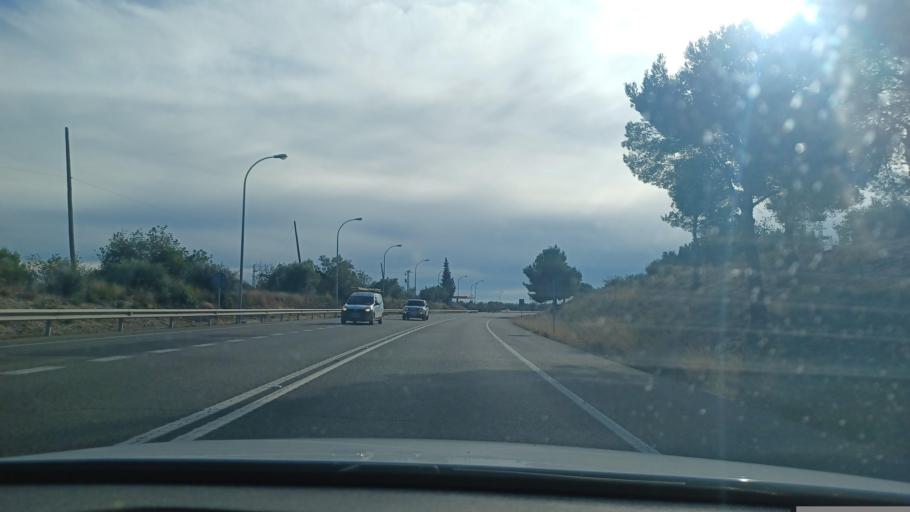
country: ES
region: Catalonia
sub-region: Provincia de Tarragona
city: L'Ampolla
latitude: 40.8401
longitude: 0.7113
